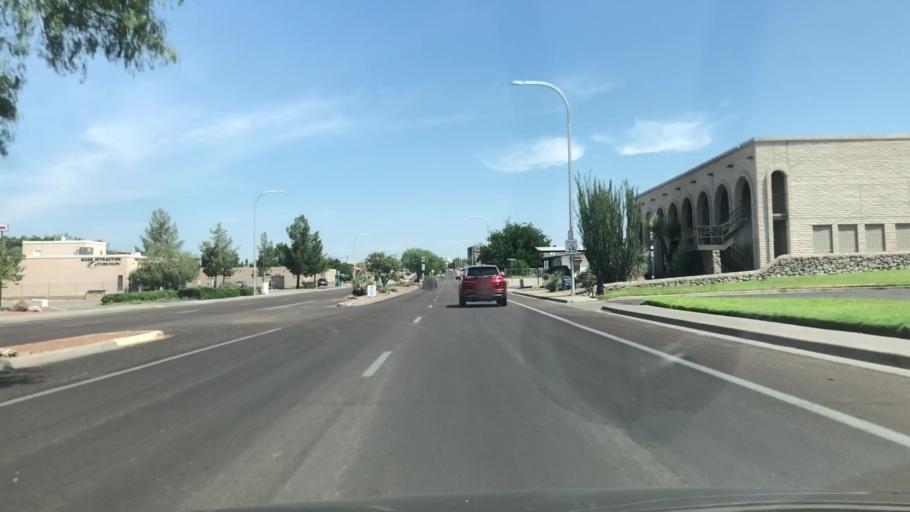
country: US
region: New Mexico
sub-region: Dona Ana County
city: University Park
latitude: 32.3006
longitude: -106.7368
